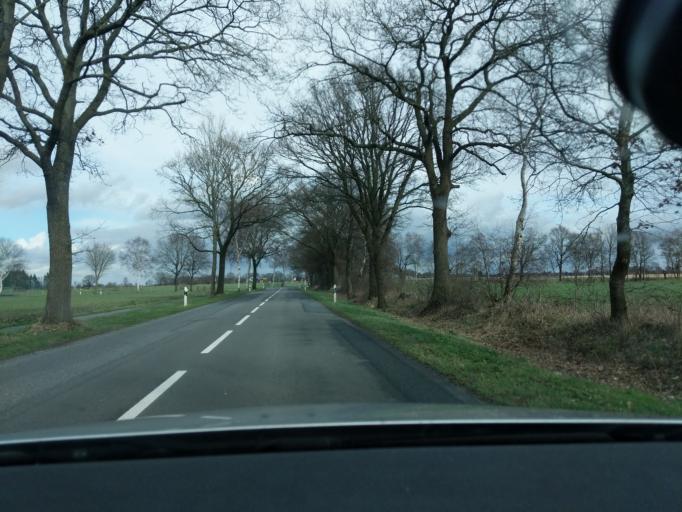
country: DE
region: Lower Saxony
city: Estorf
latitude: 53.5860
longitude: 9.2224
